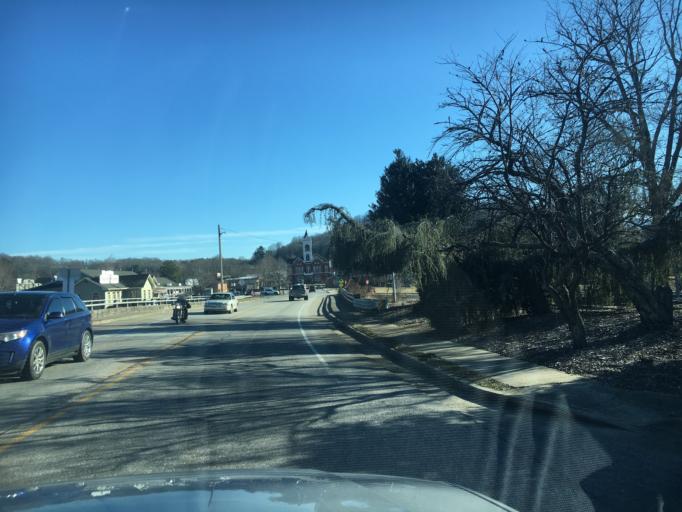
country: US
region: Georgia
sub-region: Union County
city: Blairsville
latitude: 34.8786
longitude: -83.9601
